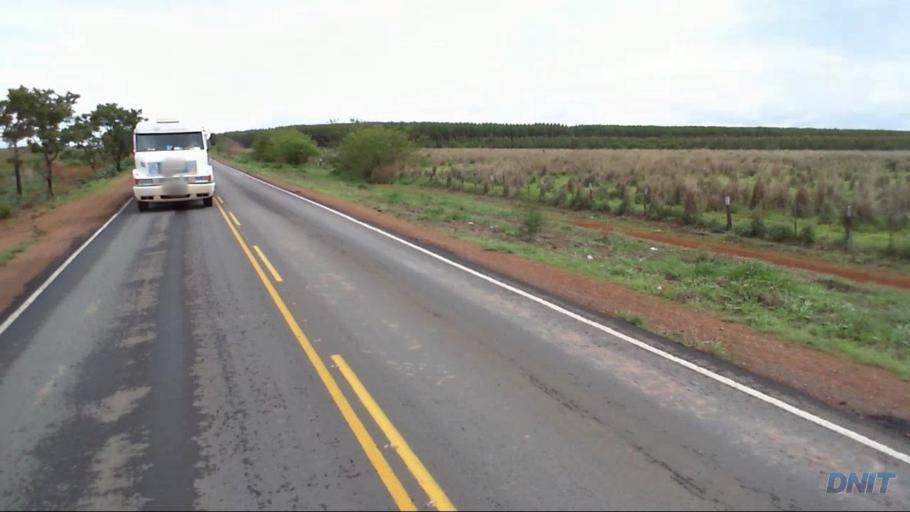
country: BR
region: Goias
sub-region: Padre Bernardo
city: Padre Bernardo
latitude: -15.2758
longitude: -48.2612
